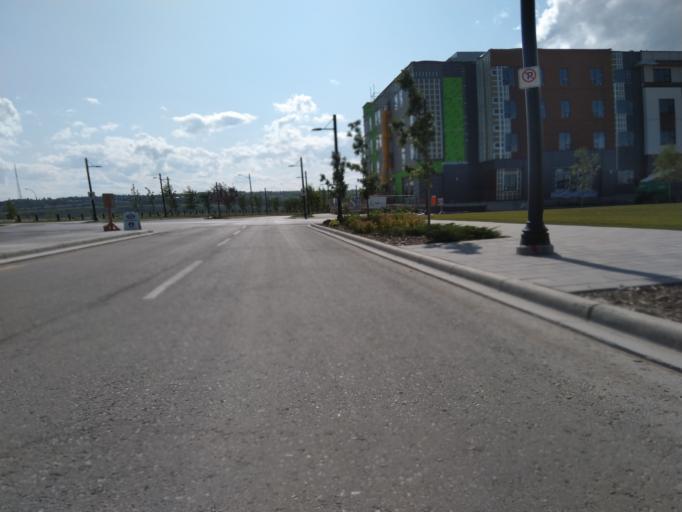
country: CA
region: Alberta
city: Calgary
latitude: 51.0772
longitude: -114.1488
